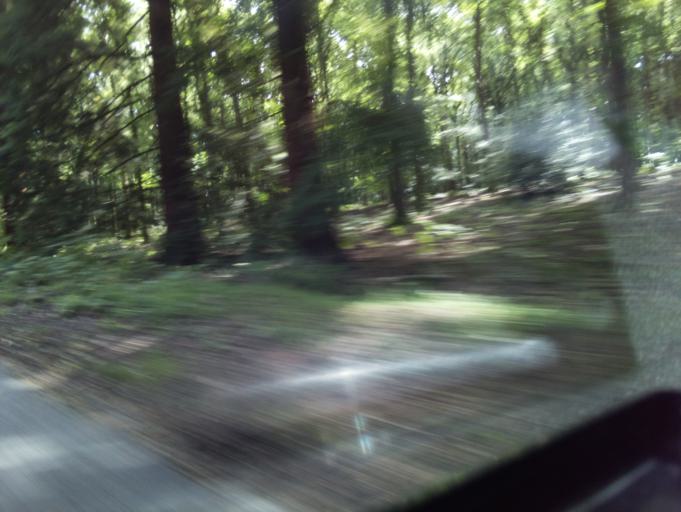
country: GB
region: England
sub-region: Gloucestershire
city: Cinderford
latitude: 51.7942
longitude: -2.4967
